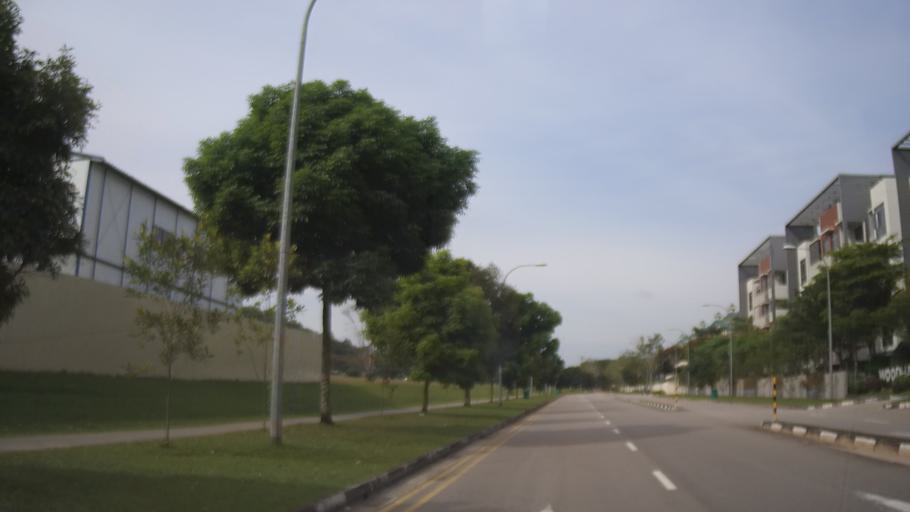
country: MY
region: Johor
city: Johor Bahru
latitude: 1.4298
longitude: 103.7851
